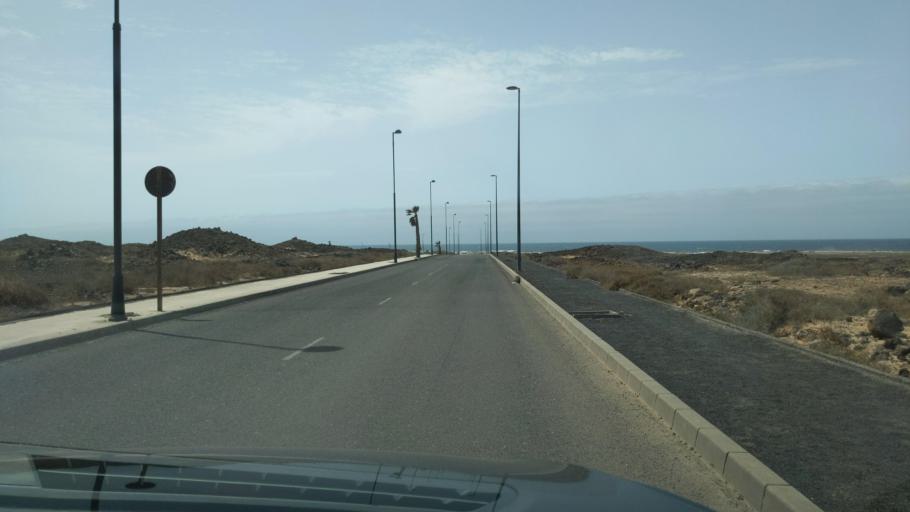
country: ES
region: Canary Islands
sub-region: Provincia de Las Palmas
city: Corralejo
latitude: 28.7370
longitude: -13.9405
